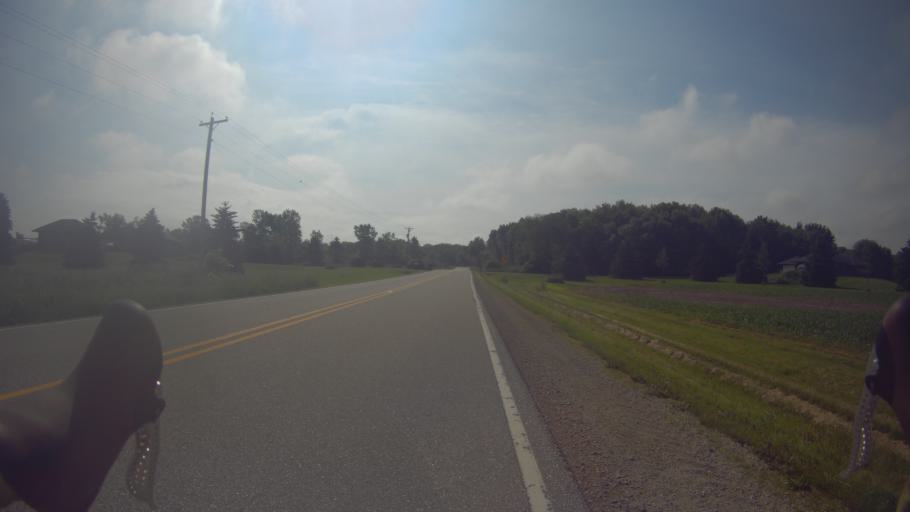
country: US
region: Wisconsin
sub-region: Dane County
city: McFarland
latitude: 43.0142
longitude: -89.2406
